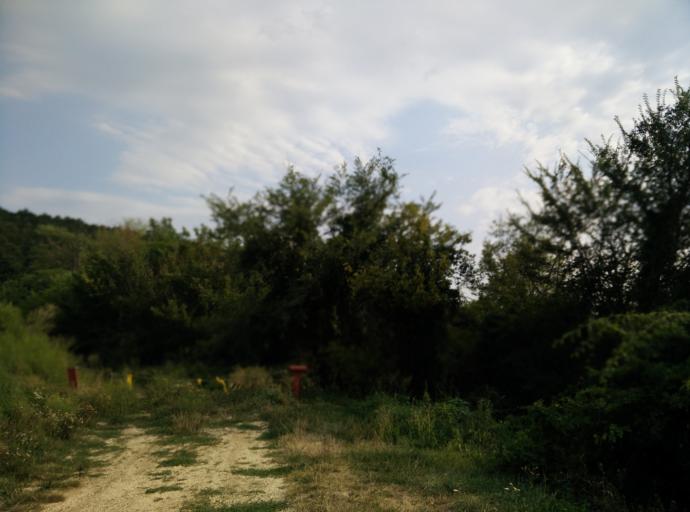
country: HU
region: Pest
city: Paty
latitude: 47.5066
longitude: 18.8449
